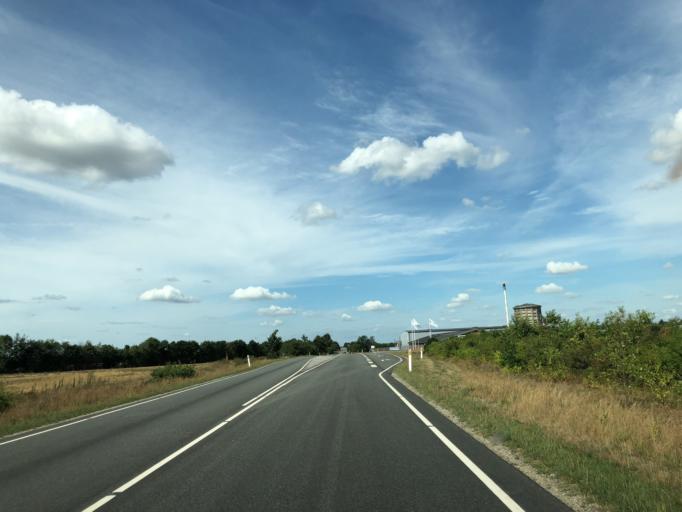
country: DK
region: Central Jutland
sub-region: Ikast-Brande Kommune
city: Bording Kirkeby
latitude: 56.1412
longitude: 9.2666
